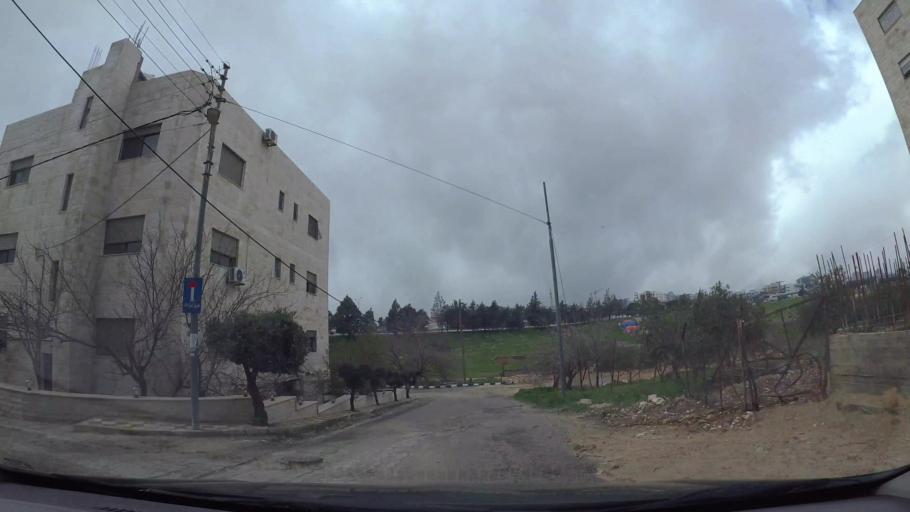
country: JO
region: Amman
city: Wadi as Sir
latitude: 31.9376
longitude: 35.8525
